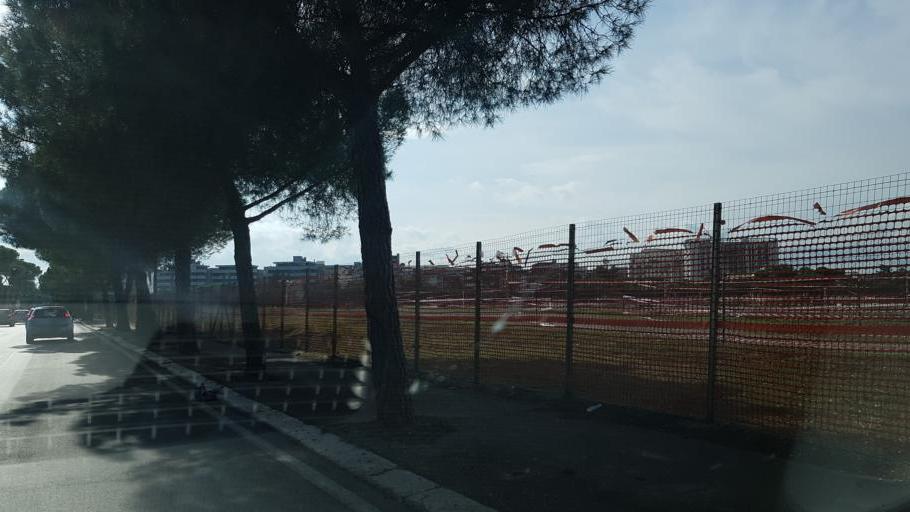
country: IT
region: Apulia
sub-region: Provincia di Foggia
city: Foggia
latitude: 41.4585
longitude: 15.5643
